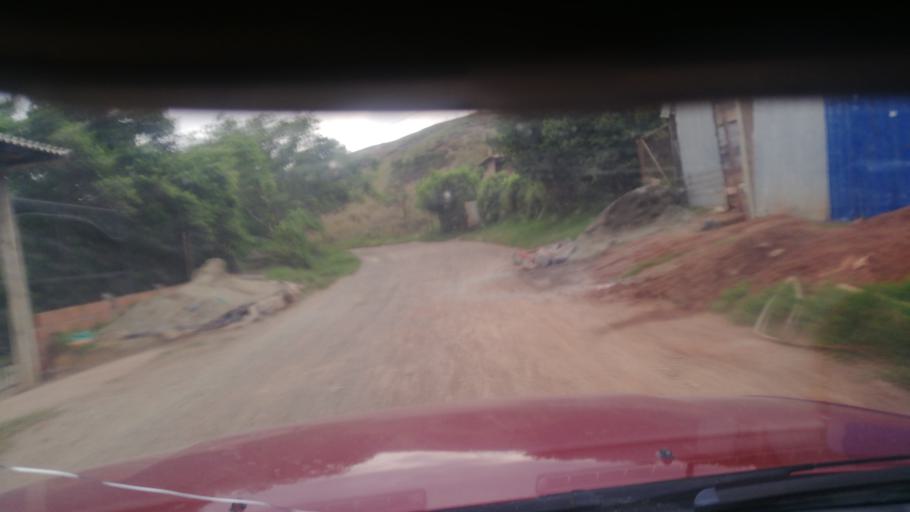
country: CO
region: Valle del Cauca
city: Cali
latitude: 3.4885
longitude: -76.5440
